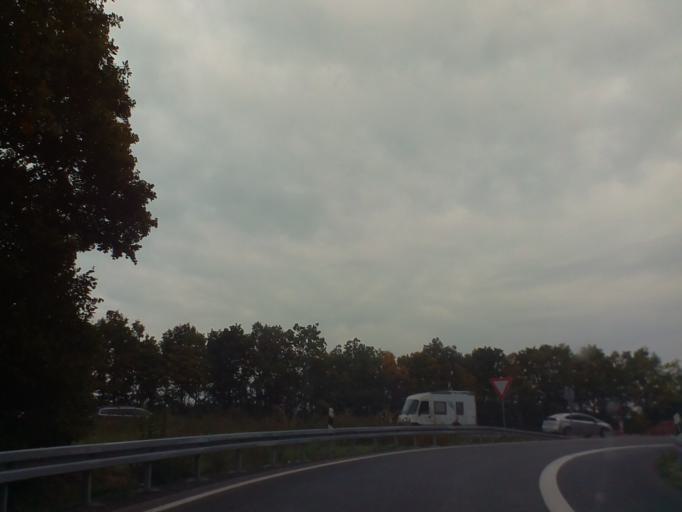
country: DE
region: Hesse
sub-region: Regierungsbezirk Kassel
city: Petersberg
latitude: 50.5830
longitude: 9.7049
